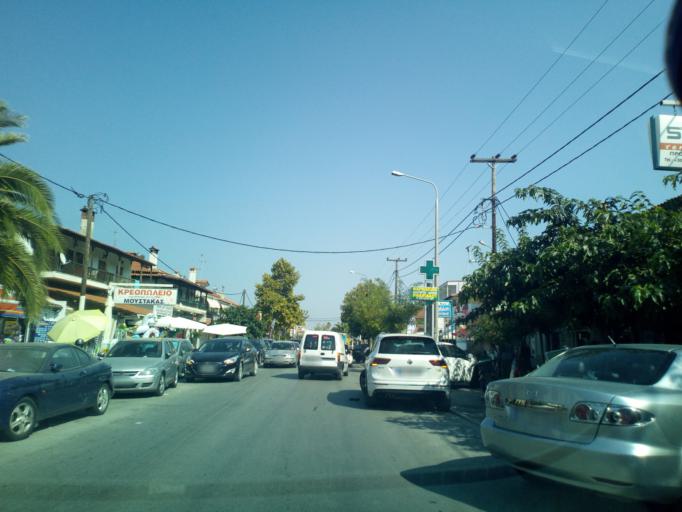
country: GR
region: Central Macedonia
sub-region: Nomos Chalkidikis
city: Pefkochori
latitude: 39.9890
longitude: 23.6123
